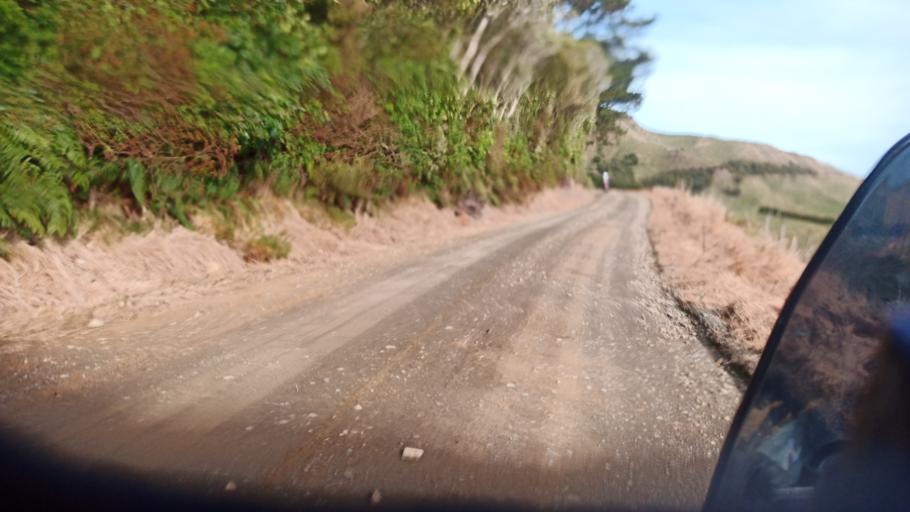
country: NZ
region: Gisborne
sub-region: Gisborne District
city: Gisborne
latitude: -38.4558
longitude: 177.5383
